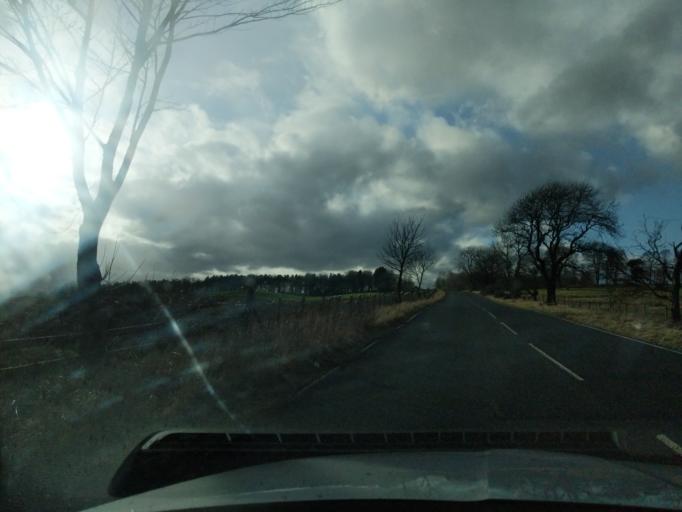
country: GB
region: England
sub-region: North Yorkshire
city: Catterick Garrison
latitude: 54.3473
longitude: -1.7628
